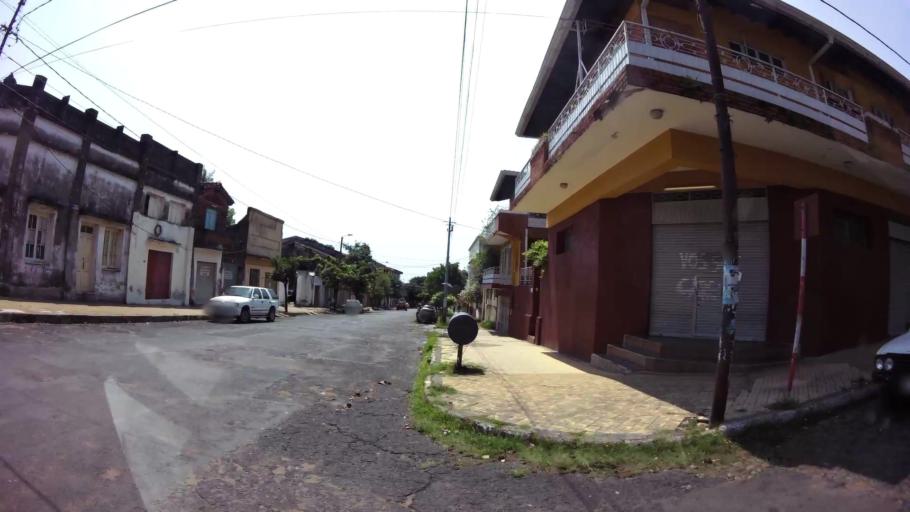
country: PY
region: Presidente Hayes
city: Nanawa
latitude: -25.2792
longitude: -57.6501
